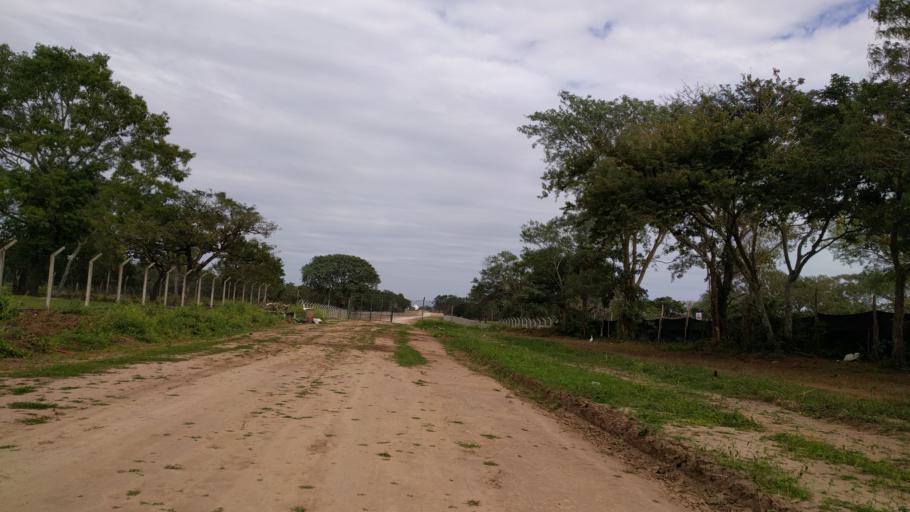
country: BO
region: Santa Cruz
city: Santa Cruz de la Sierra
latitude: -17.8145
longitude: -63.2370
